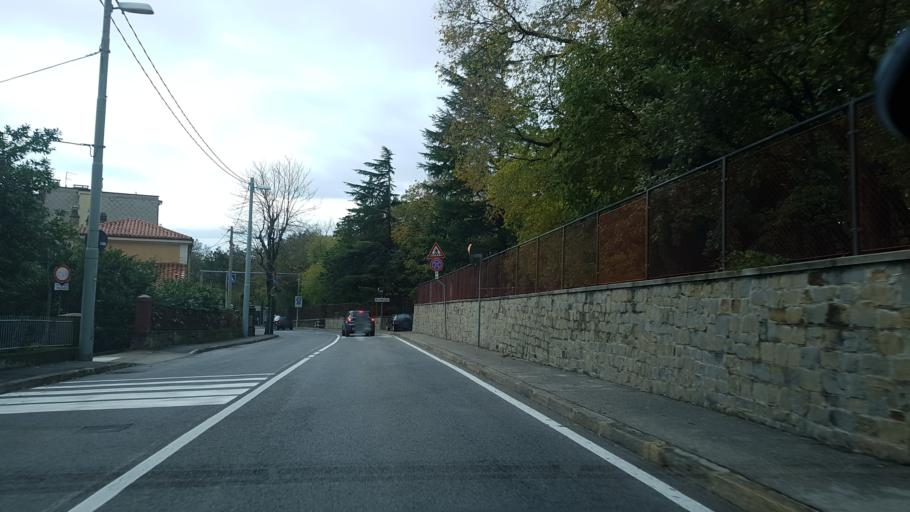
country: IT
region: Friuli Venezia Giulia
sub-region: Provincia di Trieste
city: Trieste
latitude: 45.6441
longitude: 13.8177
